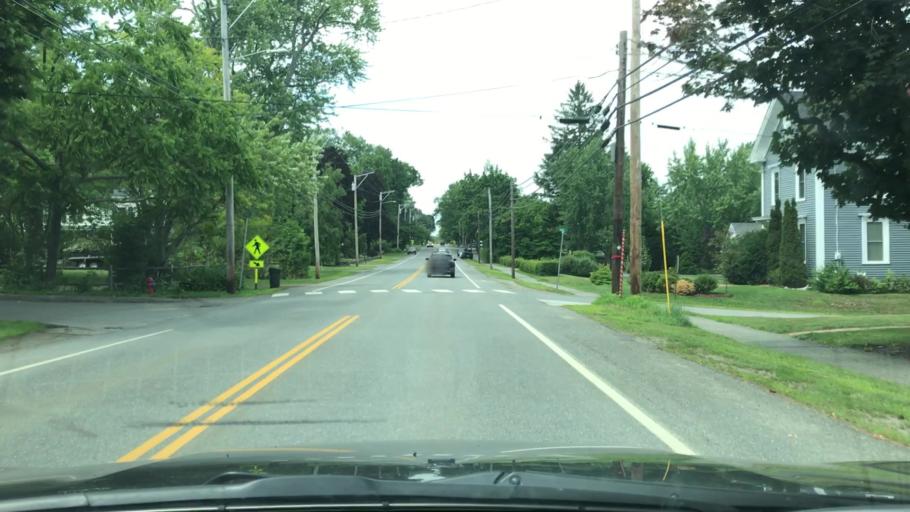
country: US
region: Maine
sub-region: Waldo County
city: Belfast
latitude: 44.4160
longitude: -68.9970
